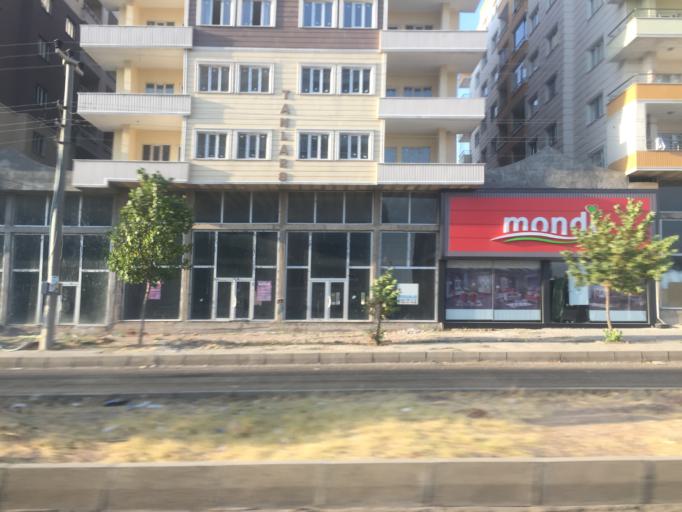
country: TR
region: Mardin
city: Midyat
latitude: 37.4347
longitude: 41.3263
